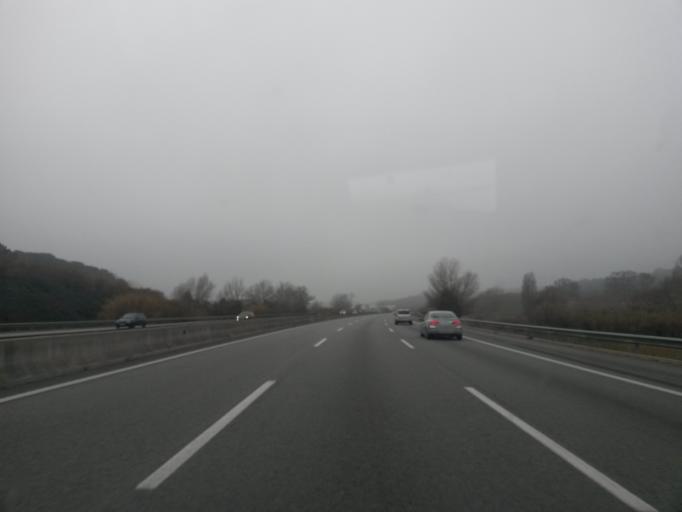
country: ES
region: Catalonia
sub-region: Provincia de Barcelona
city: Llinars del Valles
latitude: 41.6324
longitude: 2.3956
